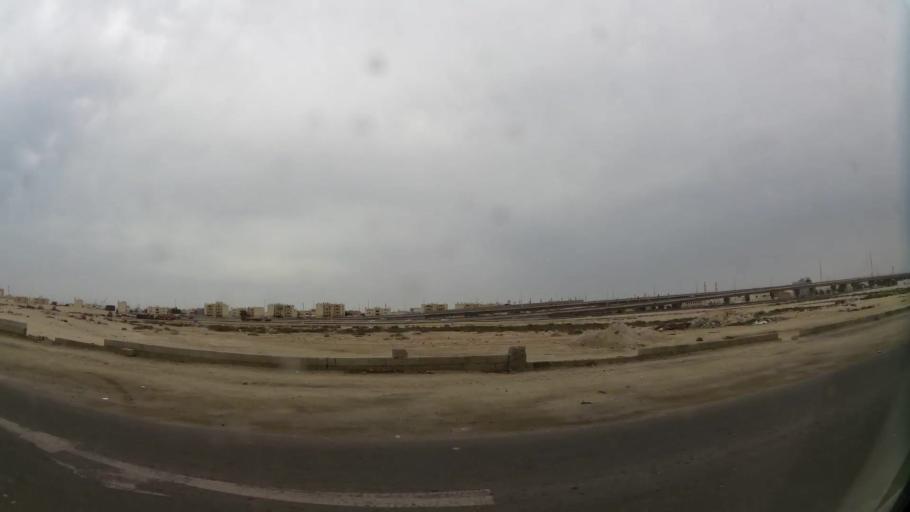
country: BH
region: Northern
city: Madinat `Isa
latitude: 26.1737
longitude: 50.5381
